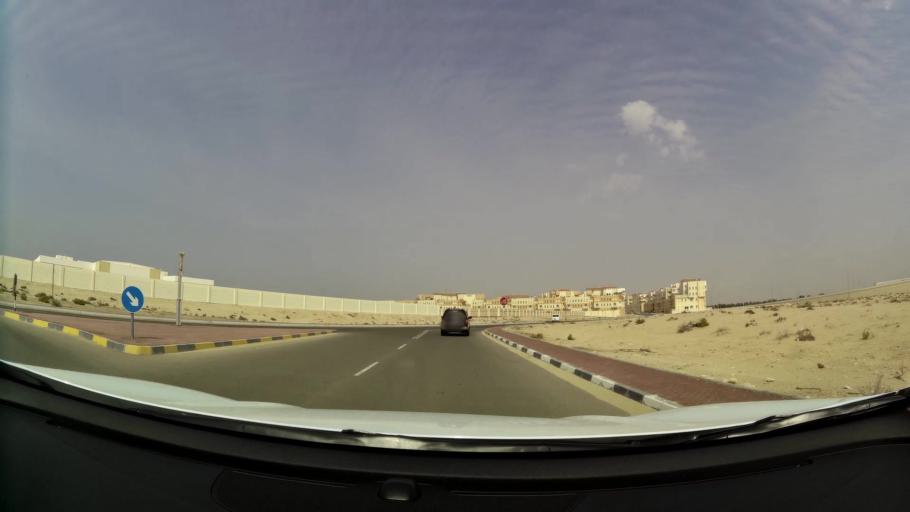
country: AE
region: Abu Dhabi
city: Abu Dhabi
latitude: 24.5483
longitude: 54.6883
